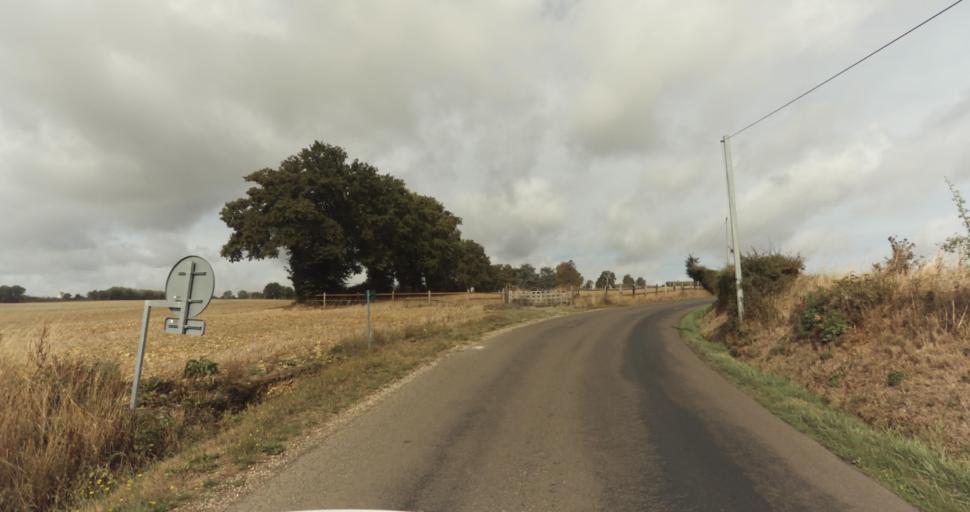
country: FR
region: Lower Normandy
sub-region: Departement de l'Orne
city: Gace
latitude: 48.8391
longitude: 0.3778
